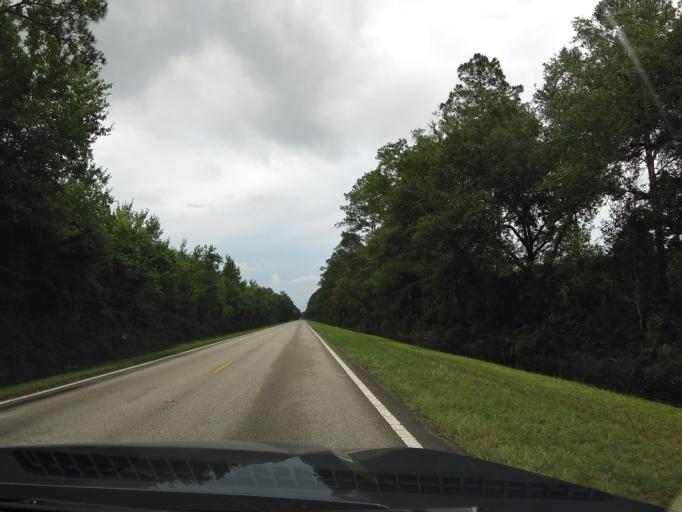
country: US
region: Florida
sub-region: Saint Johns County
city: Saint Augustine South
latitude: 29.8570
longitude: -81.4410
